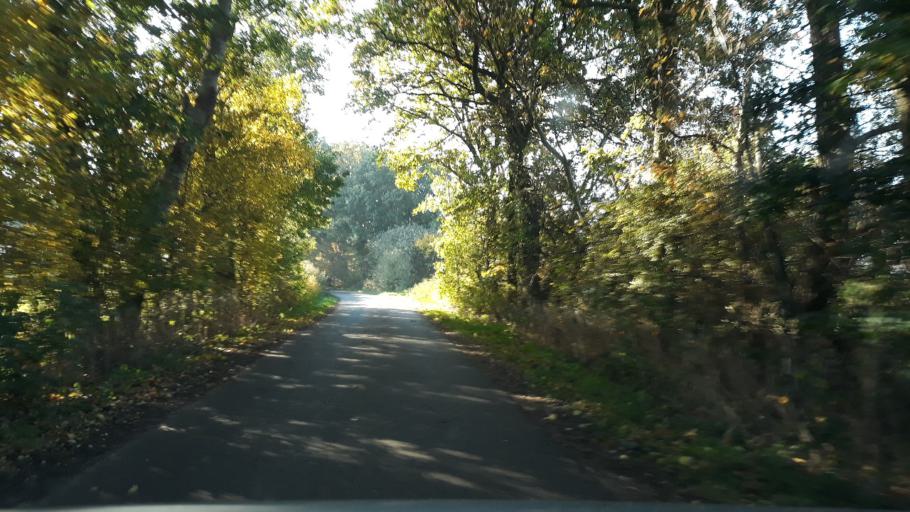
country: DE
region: Schleswig-Holstein
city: Borm
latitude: 54.4041
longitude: 9.3941
